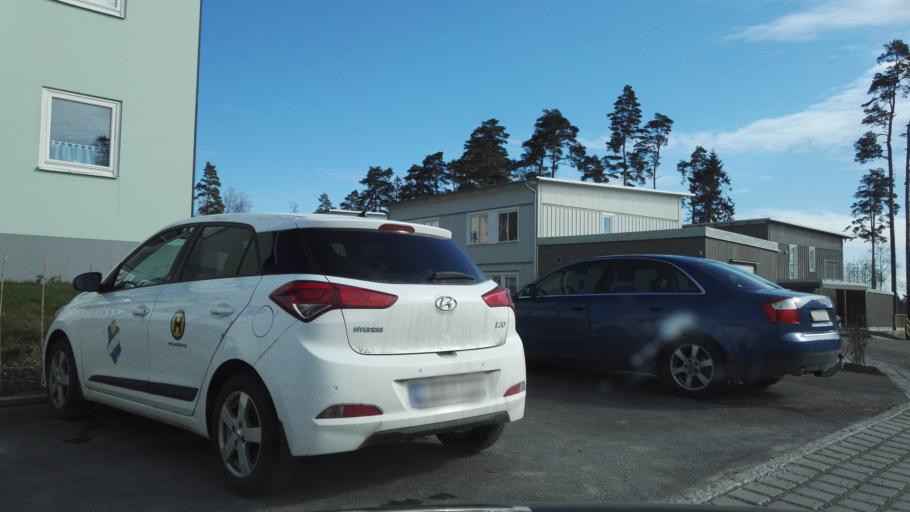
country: SE
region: Kronoberg
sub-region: Vaxjo Kommun
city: Vaexjoe
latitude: 56.9175
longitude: 14.8040
